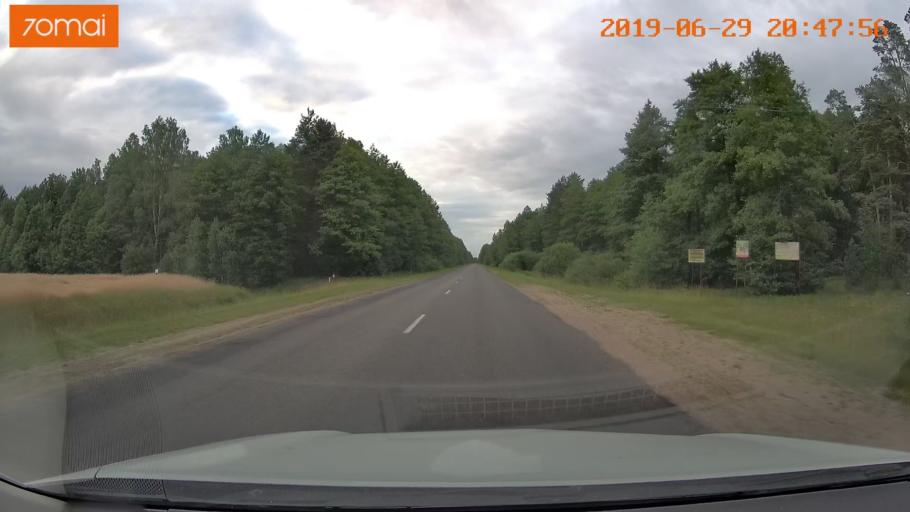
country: BY
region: Brest
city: Hantsavichy
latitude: 52.6441
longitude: 26.3165
